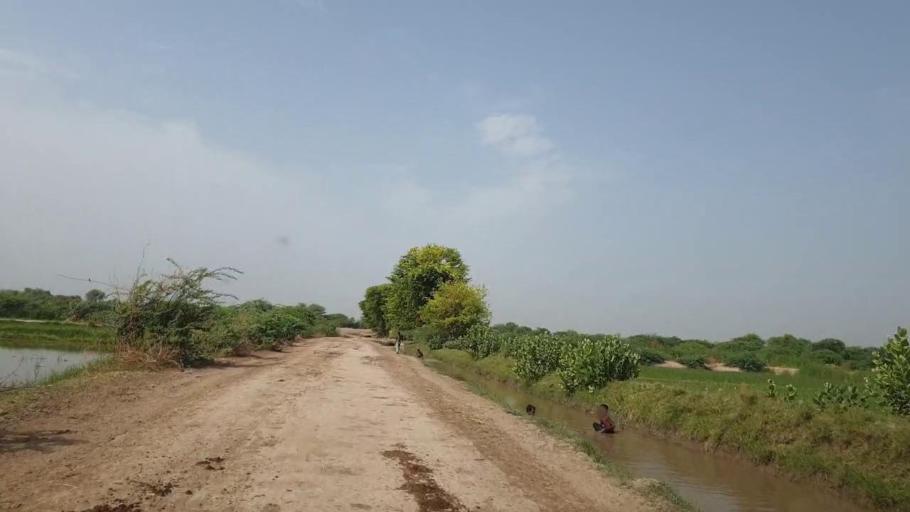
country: PK
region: Sindh
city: Lakhi
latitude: 27.7966
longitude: 68.7104
